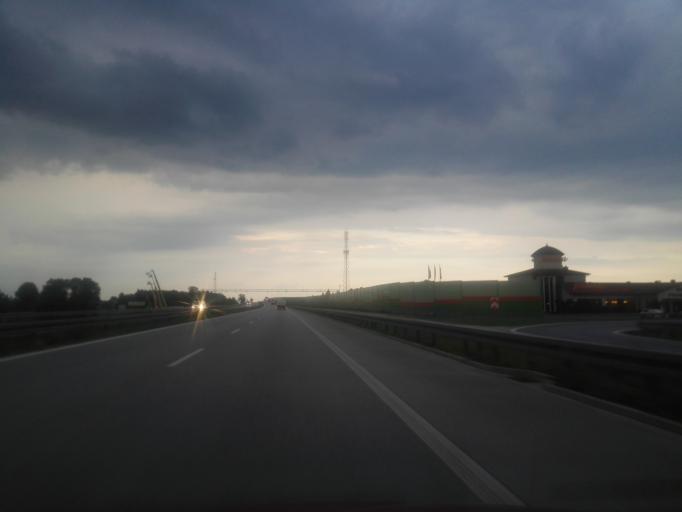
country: PL
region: Lodz Voivodeship
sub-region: Piotrkow Trybunalski
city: Piotrkow Trybunalski
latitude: 51.4419
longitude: 19.6801
